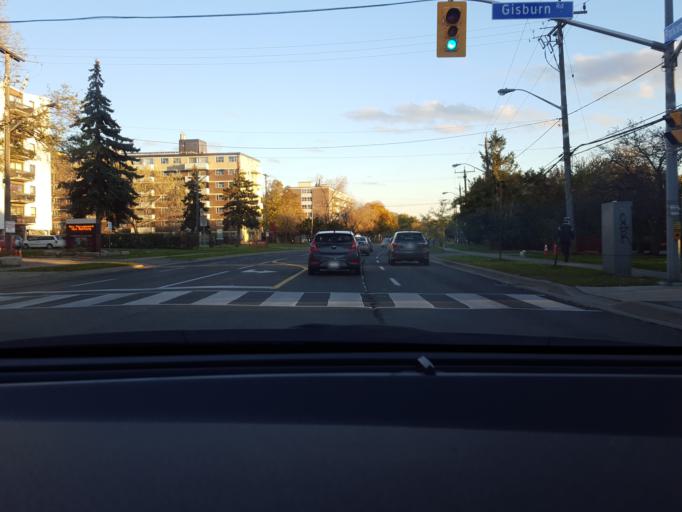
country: CA
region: Ontario
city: Scarborough
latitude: 43.7601
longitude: -79.3221
